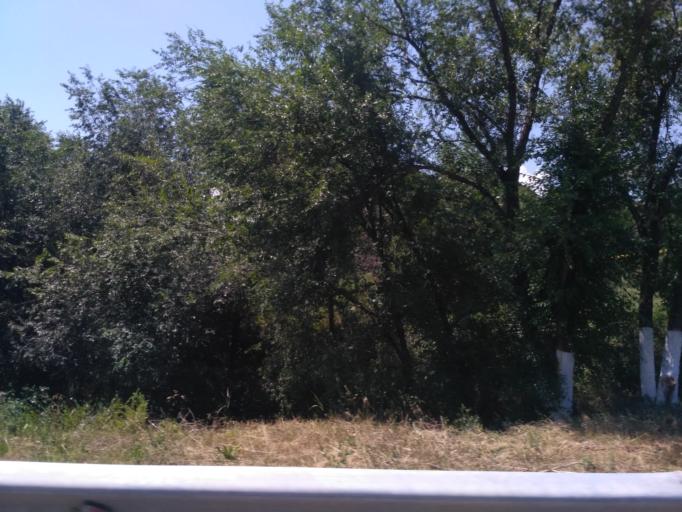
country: KZ
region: Almaty Oblysy
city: Burunday
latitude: 43.1661
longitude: 76.6016
